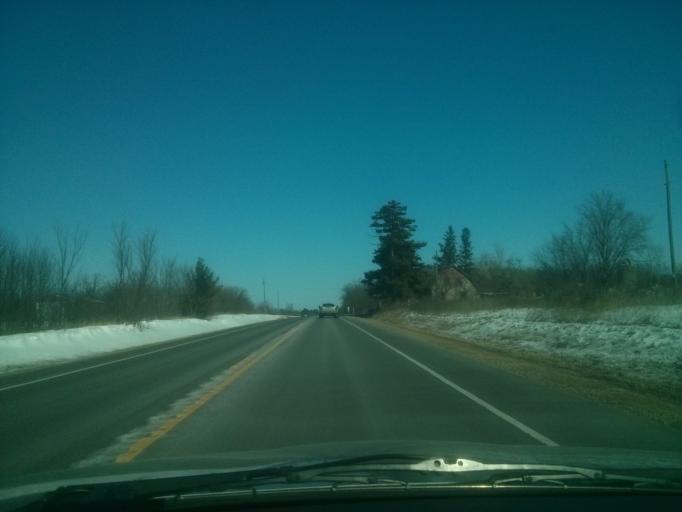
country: US
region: Wisconsin
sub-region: Polk County
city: Clear Lake
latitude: 45.1925
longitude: -92.2835
